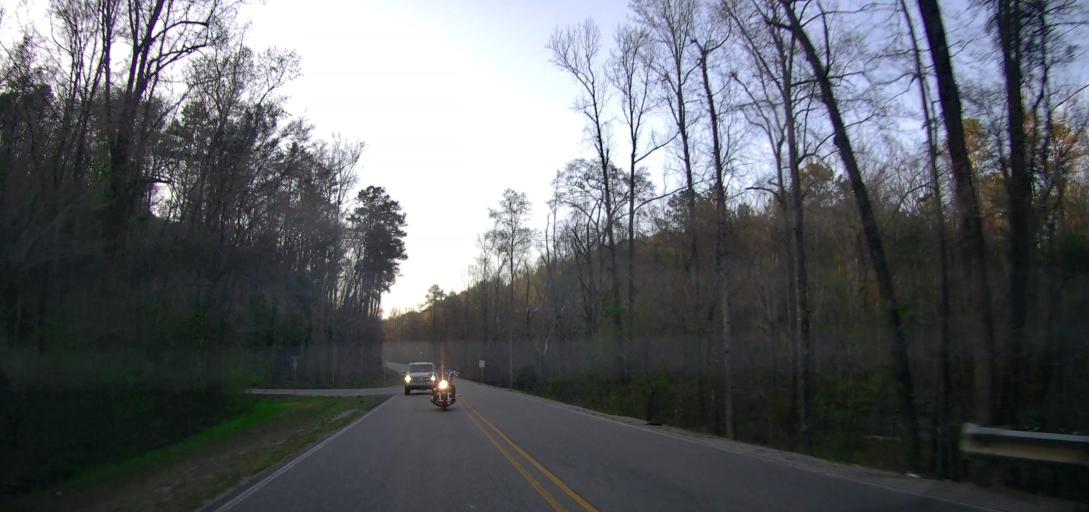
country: US
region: Alabama
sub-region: Shelby County
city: Chelsea
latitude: 33.3477
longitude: -86.6422
